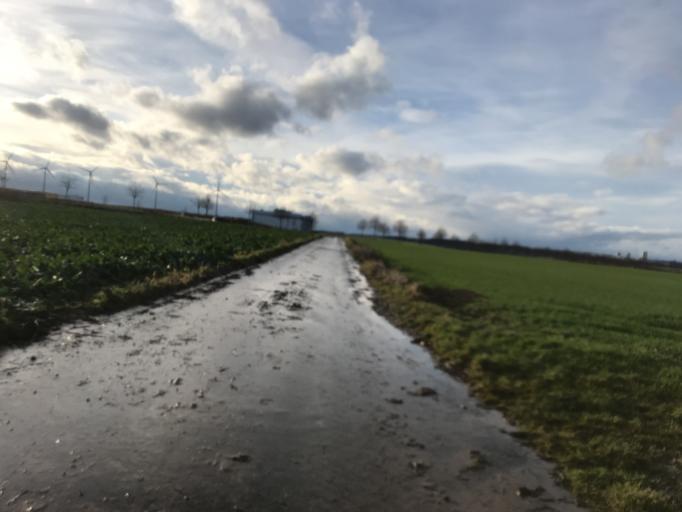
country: DE
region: Rheinland-Pfalz
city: Gau-Bischofsheim
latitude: 49.9502
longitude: 8.2623
